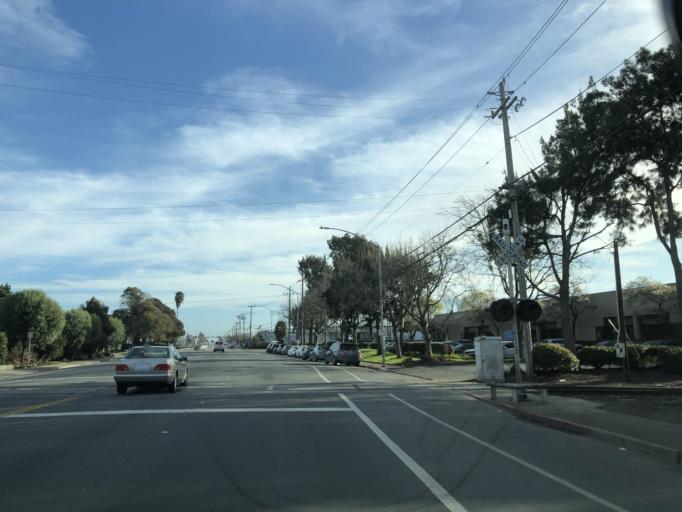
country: US
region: California
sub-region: Alameda County
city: San Leandro
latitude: 37.7123
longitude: -122.1851
